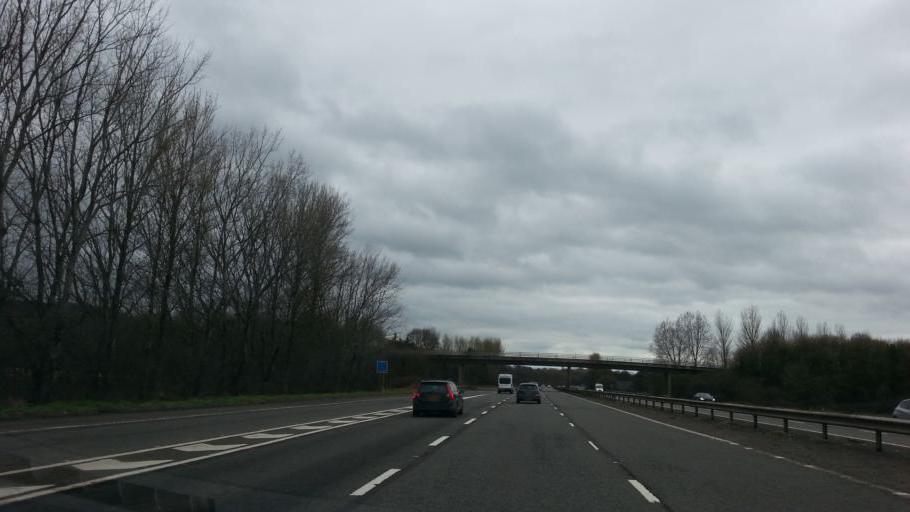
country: GB
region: England
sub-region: Somerset
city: Taunton
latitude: 50.9759
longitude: -3.1521
